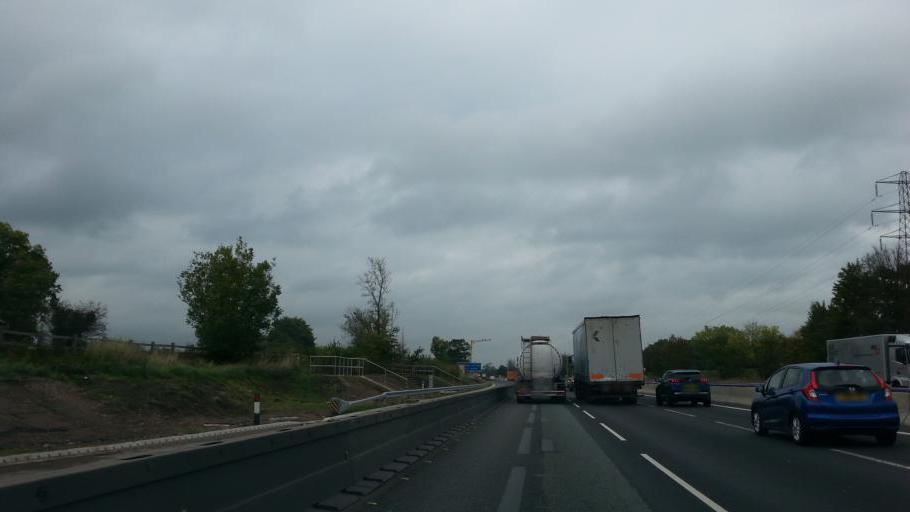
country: GB
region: England
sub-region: Cheshire East
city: Knutsford
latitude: 53.2806
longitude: -2.3962
